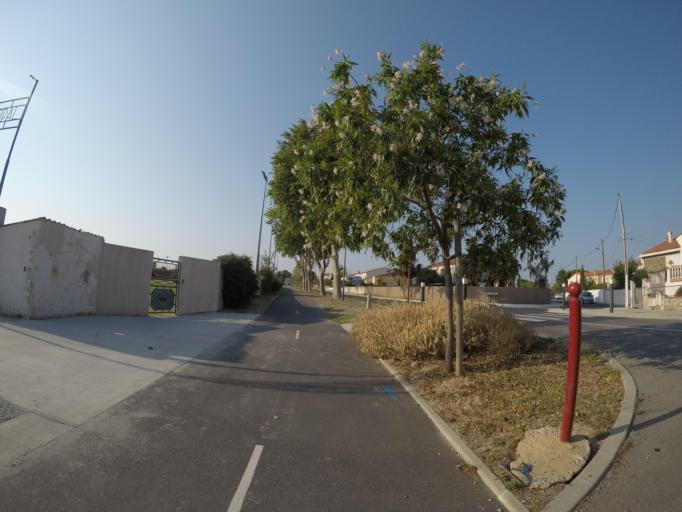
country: FR
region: Languedoc-Roussillon
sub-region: Departement des Pyrenees-Orientales
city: Toulouges
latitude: 42.6649
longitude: 2.8324
